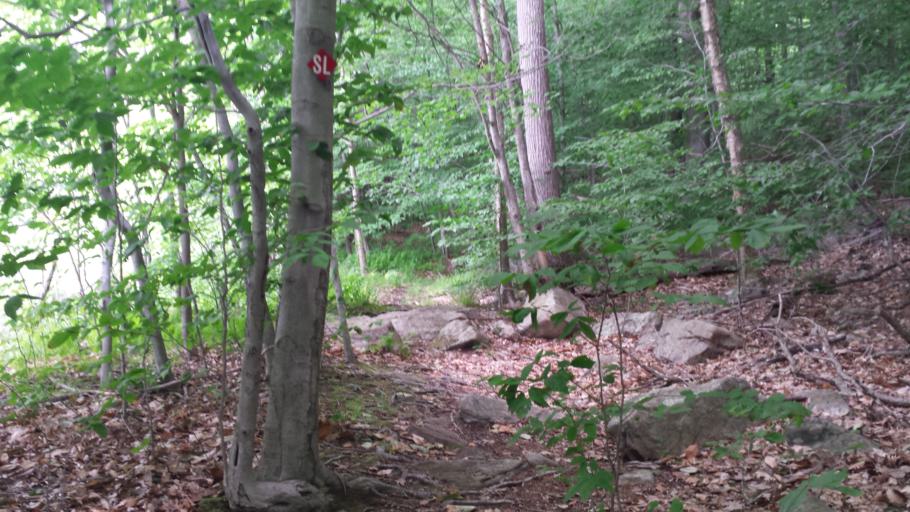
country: US
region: New York
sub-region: Putnam County
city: Peach Lake
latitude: 41.3109
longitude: -73.5678
